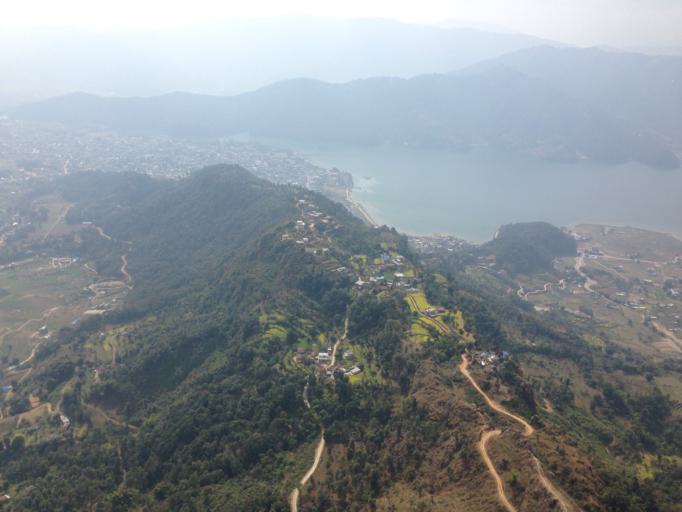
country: NP
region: Western Region
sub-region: Gandaki Zone
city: Pokhara
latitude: 28.2353
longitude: 83.9684
